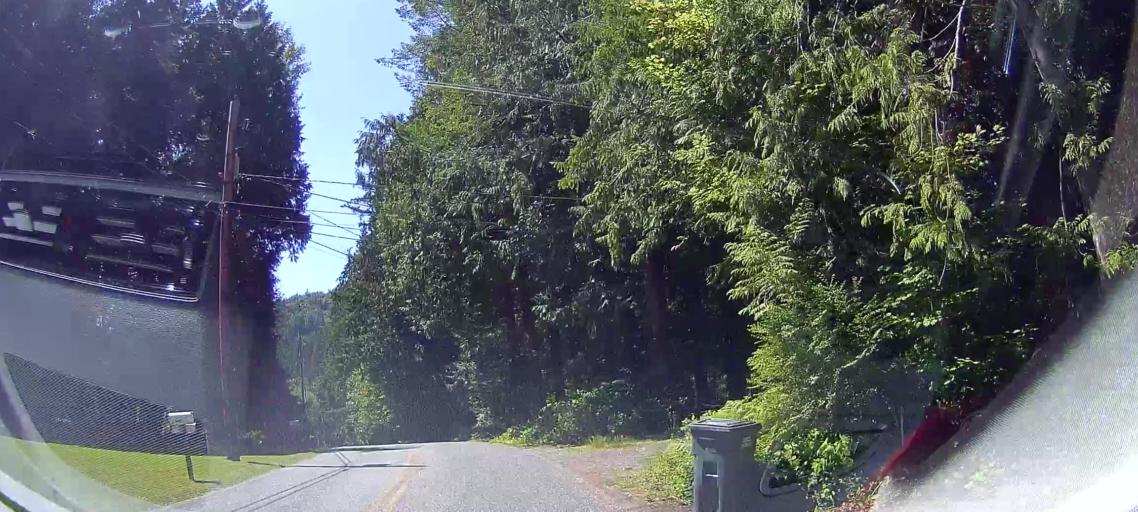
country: US
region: Washington
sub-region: Whatcom County
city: Sudden Valley
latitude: 48.6454
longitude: -122.3257
